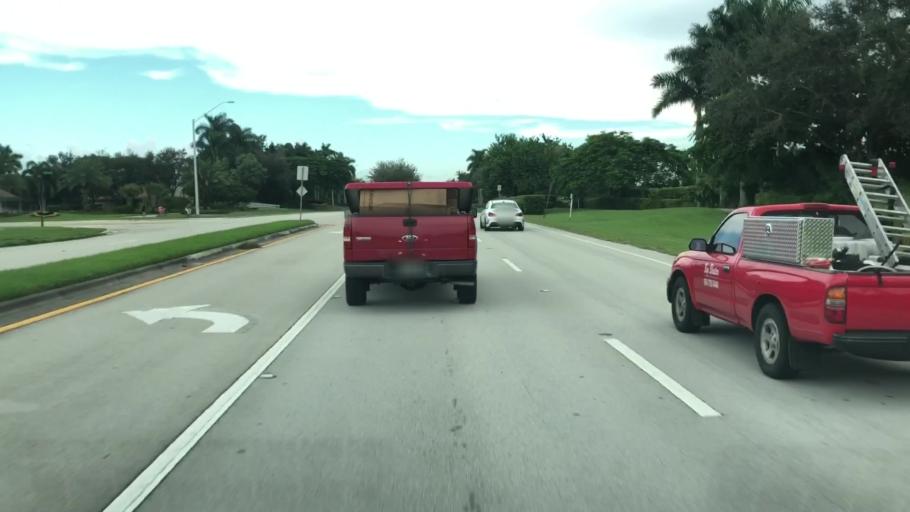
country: US
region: Florida
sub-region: Broward County
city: Parkland
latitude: 26.3144
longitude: -80.2789
